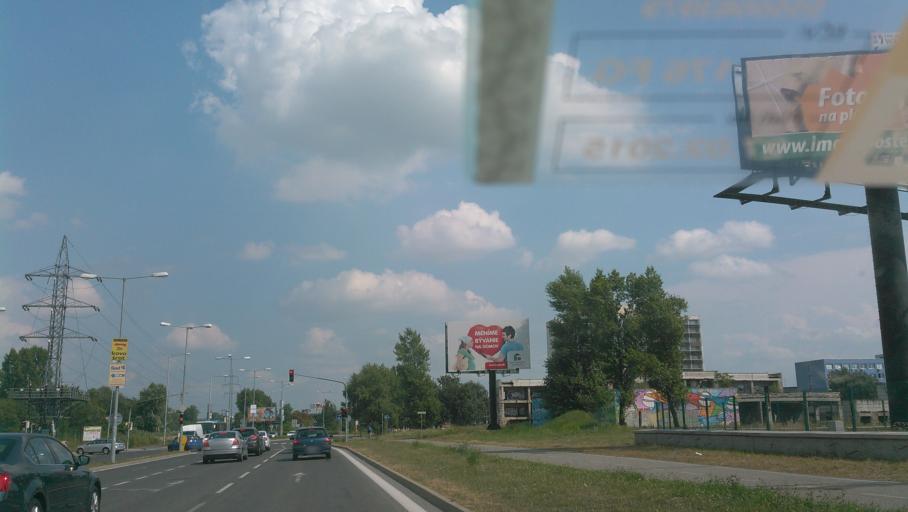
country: SK
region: Bratislavsky
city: Bratislava
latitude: 48.1419
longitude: 17.1400
